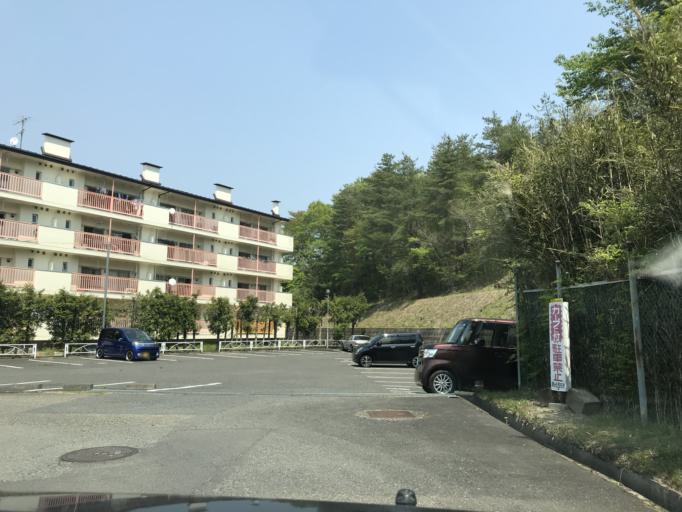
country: JP
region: Iwate
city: Ichinoseki
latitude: 38.9138
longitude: 141.1487
